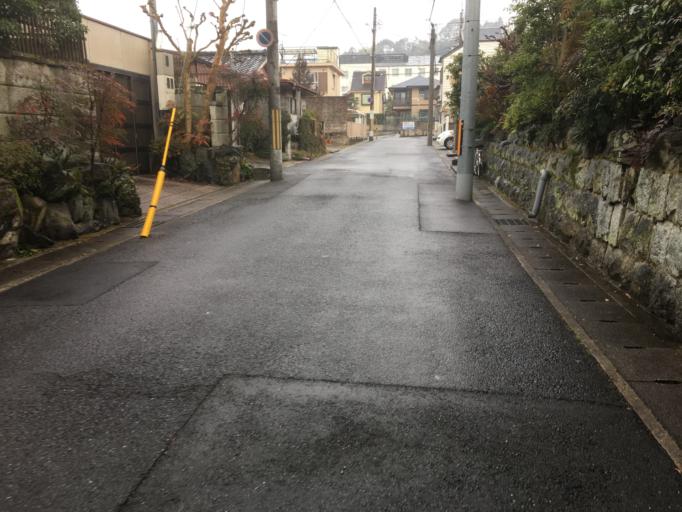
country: JP
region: Kyoto
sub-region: Kyoto-shi
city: Kamigyo-ku
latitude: 35.0312
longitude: 135.7940
